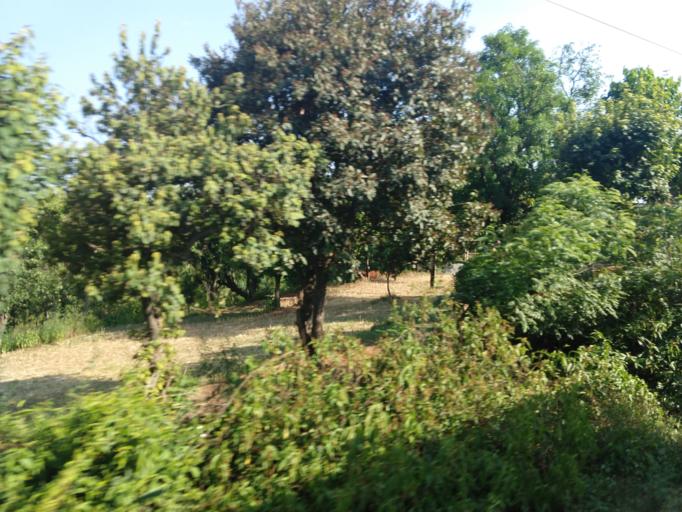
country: IN
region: Himachal Pradesh
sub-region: Chamba
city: Chowari
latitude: 32.3731
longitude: 75.9239
